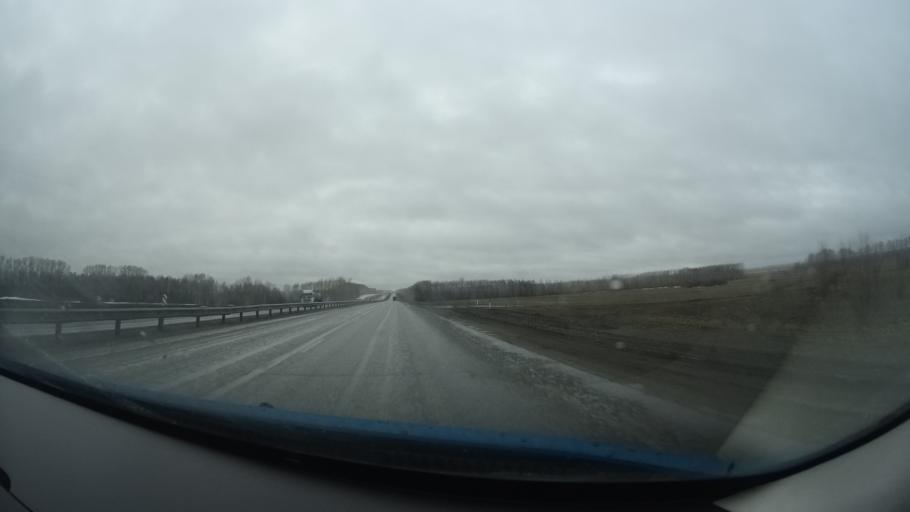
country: RU
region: Bashkortostan
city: Dmitriyevka
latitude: 54.7107
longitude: 55.2175
